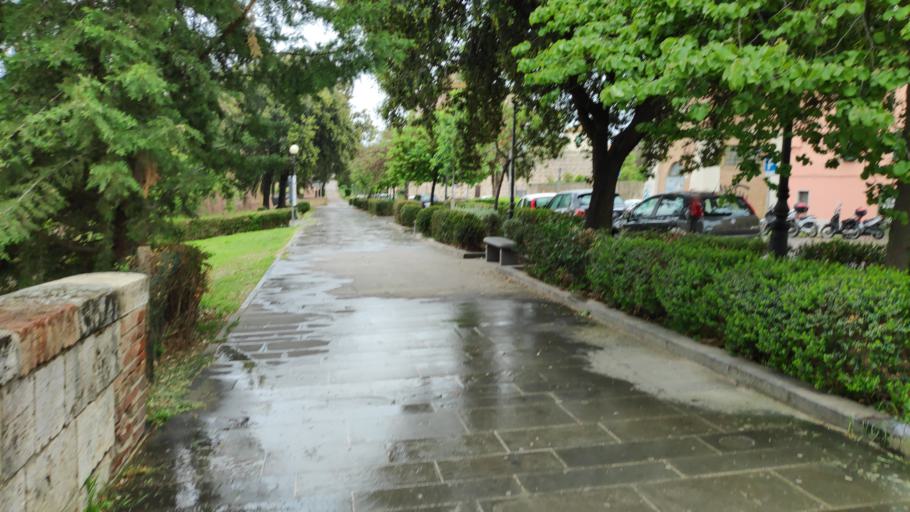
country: IT
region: Tuscany
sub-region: Provincia di Grosseto
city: Grosseto
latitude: 42.7617
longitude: 11.1161
